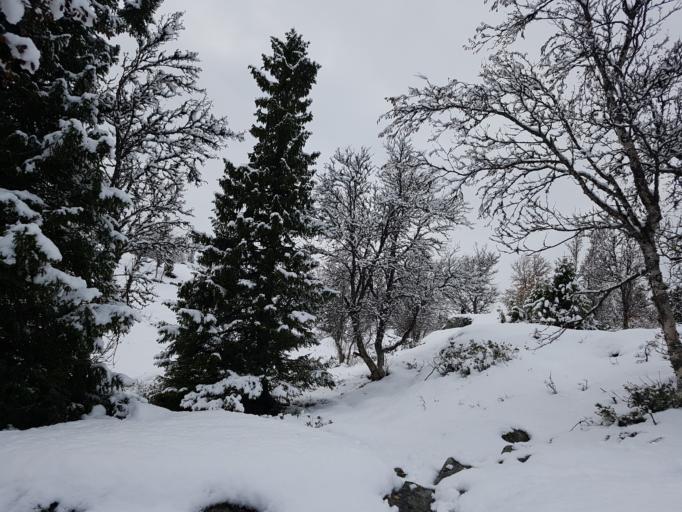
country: NO
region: Oppland
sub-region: Sel
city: Otta
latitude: 61.8048
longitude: 9.6769
